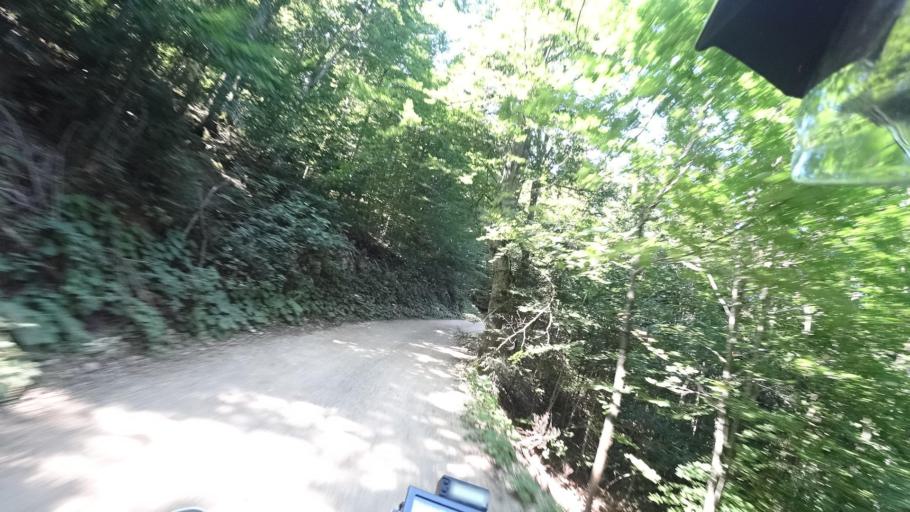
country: HR
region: Licko-Senjska
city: Popovaca
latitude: 44.5769
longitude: 15.1951
